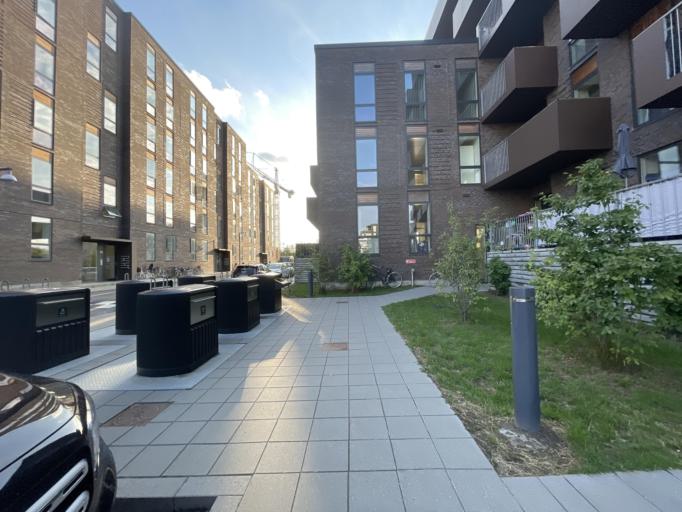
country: DK
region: Capital Region
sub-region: Rodovre Kommune
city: Rodovre
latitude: 55.6763
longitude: 12.4366
